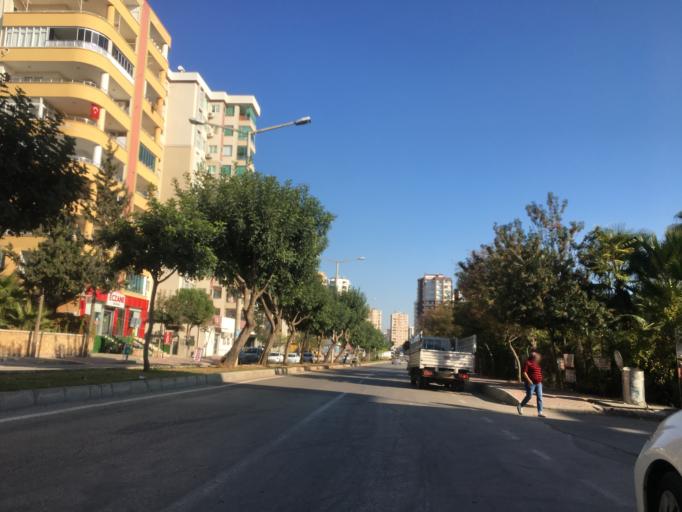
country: TR
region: Adana
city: Seyhan
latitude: 37.0290
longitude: 35.2685
